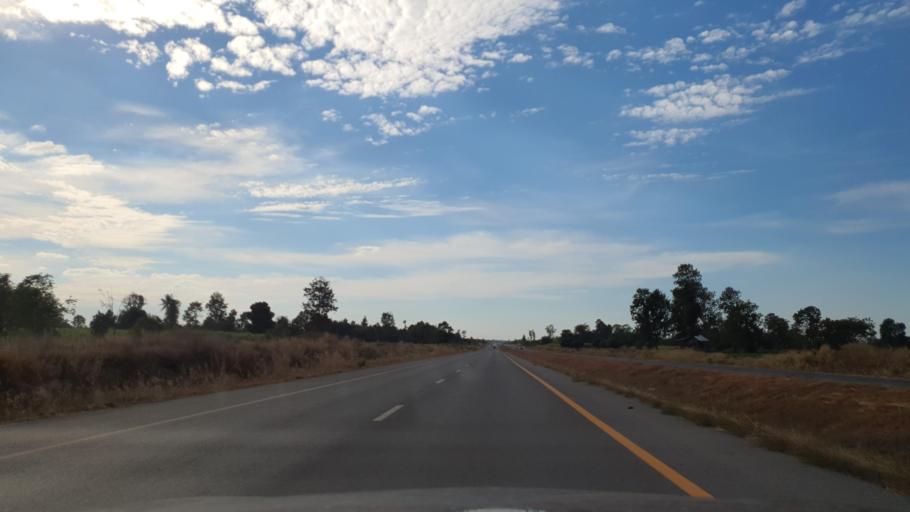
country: TH
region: Roi Et
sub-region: Amphoe Pho Chai
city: Pho Chai
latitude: 16.4132
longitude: 103.7792
